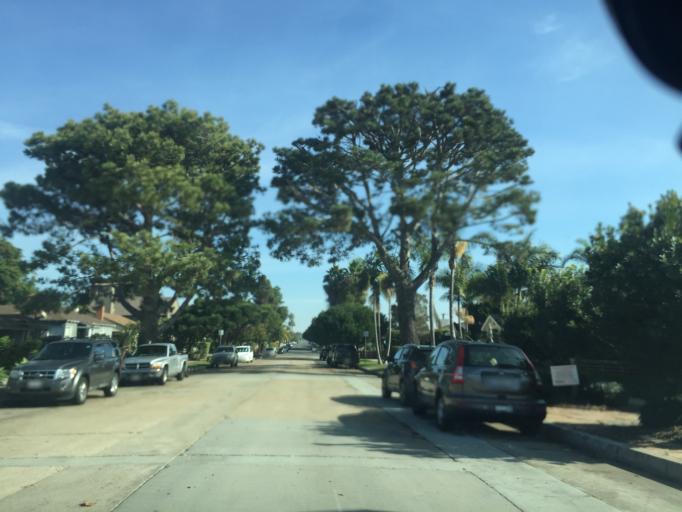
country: US
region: California
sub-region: San Diego County
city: La Jolla
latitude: 32.7927
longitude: -117.2500
